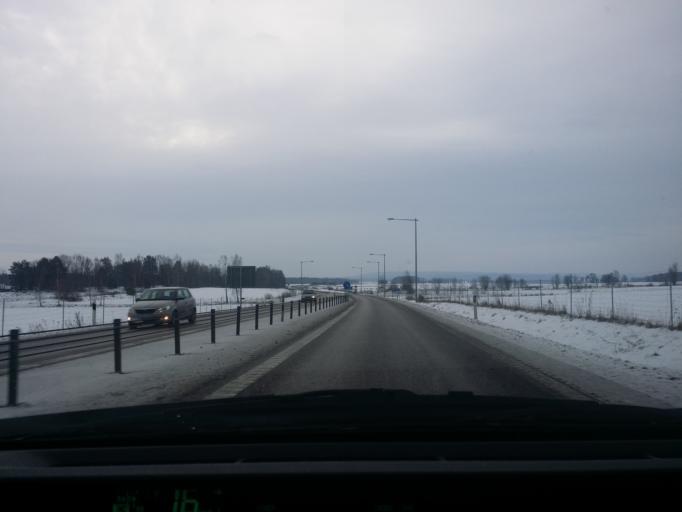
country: SE
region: Vaestra Goetaland
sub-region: Mariestads Kommun
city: Mariestad
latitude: 58.5937
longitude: 13.7978
